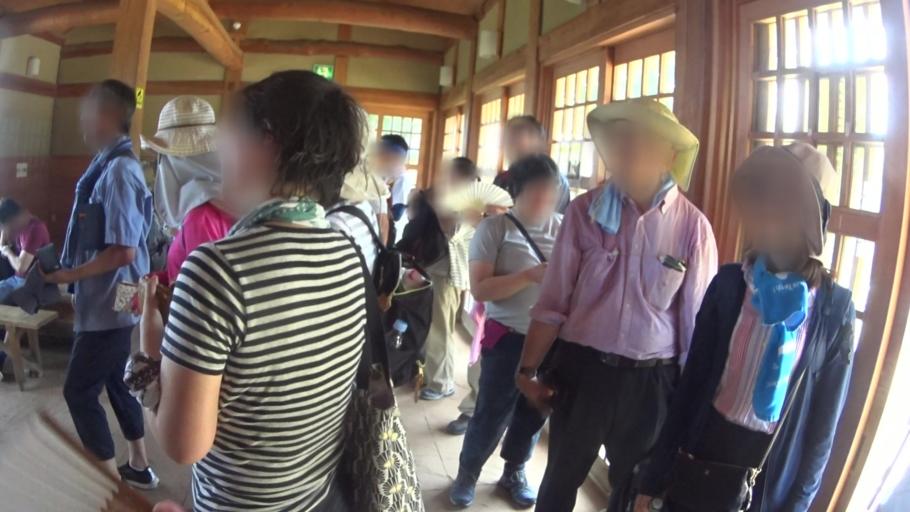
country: JP
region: Gunma
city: Ota
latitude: 36.3154
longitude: 139.3770
